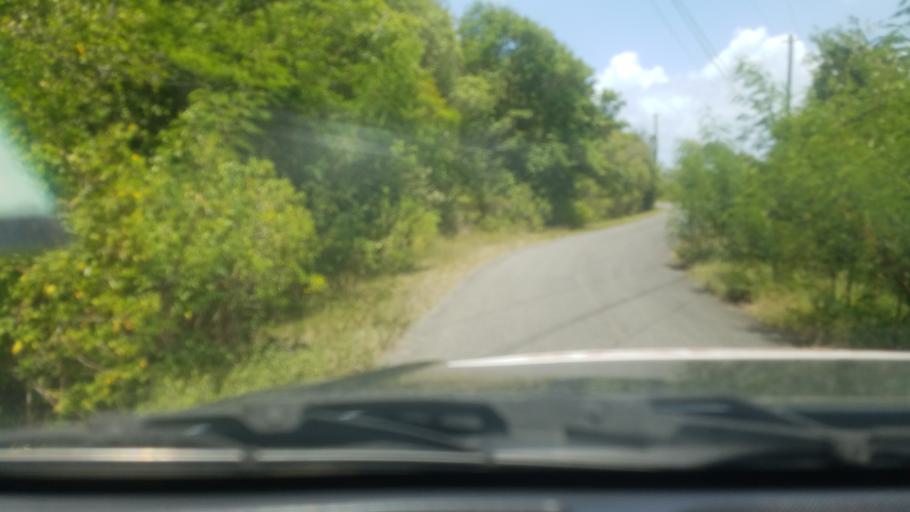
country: LC
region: Vieux-Fort
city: Vieux Fort
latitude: 13.7124
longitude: -60.9433
